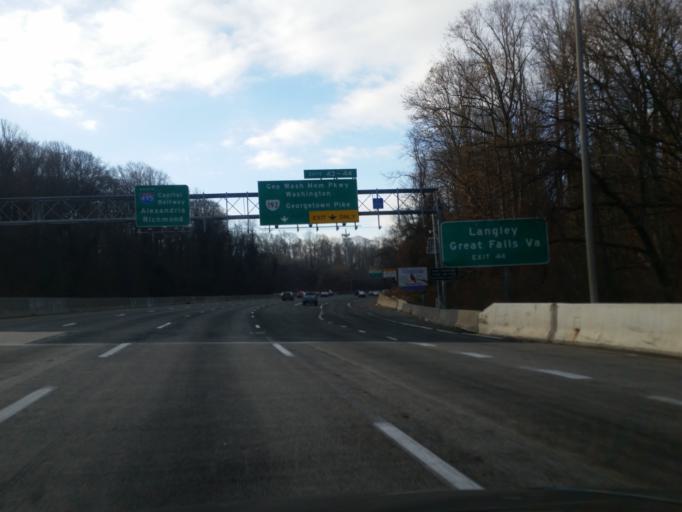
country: US
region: Maryland
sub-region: Montgomery County
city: Cabin John
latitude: 38.9675
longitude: -77.1800
